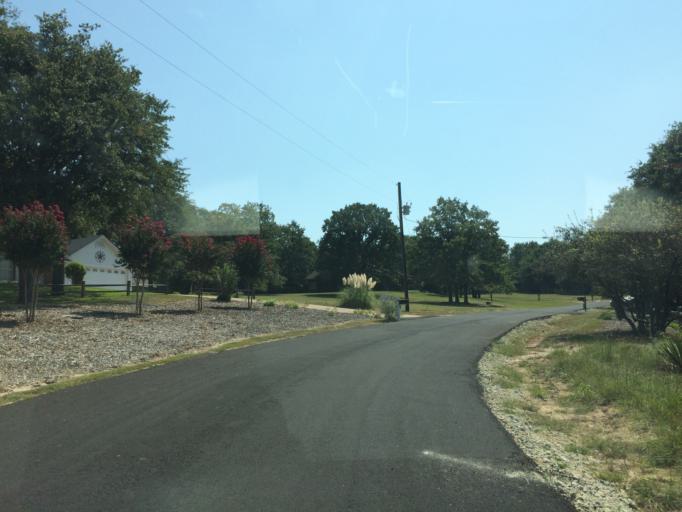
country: US
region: Texas
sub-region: Wood County
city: Hawkins
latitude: 32.7197
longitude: -95.1771
